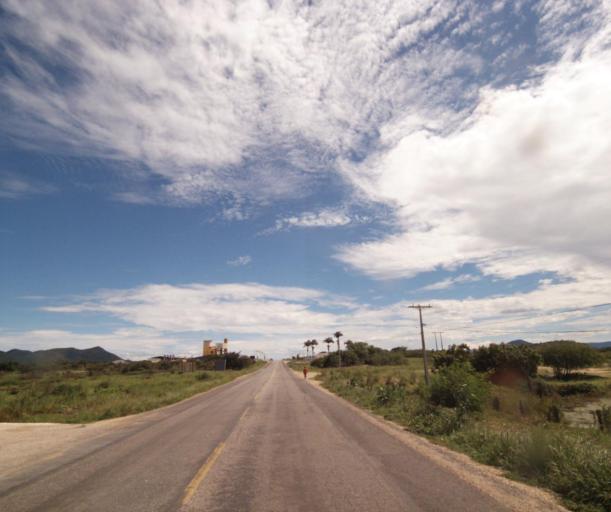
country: BR
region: Bahia
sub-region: Guanambi
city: Guanambi
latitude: -14.2533
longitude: -42.7820
